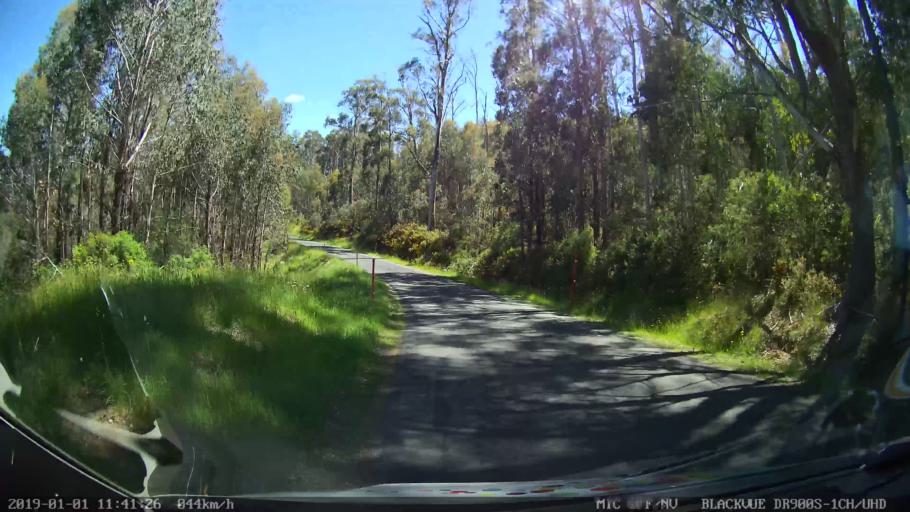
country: AU
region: New South Wales
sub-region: Snowy River
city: Jindabyne
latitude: -35.9142
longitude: 148.3906
